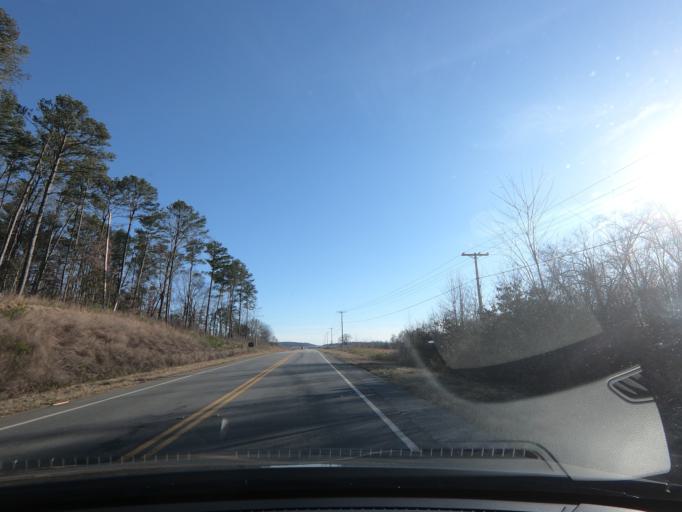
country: US
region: Georgia
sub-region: Gordon County
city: Calhoun
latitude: 34.4476
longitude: -84.9143
